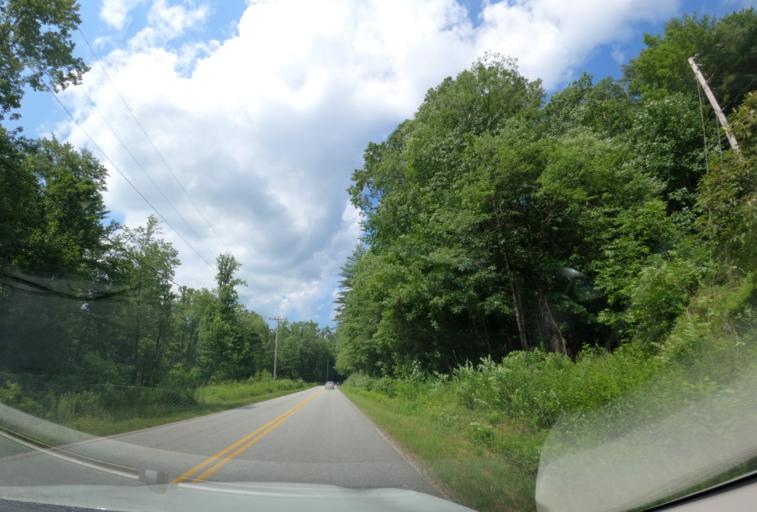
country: US
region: North Carolina
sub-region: Transylvania County
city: Brevard
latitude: 35.0885
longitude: -82.9807
